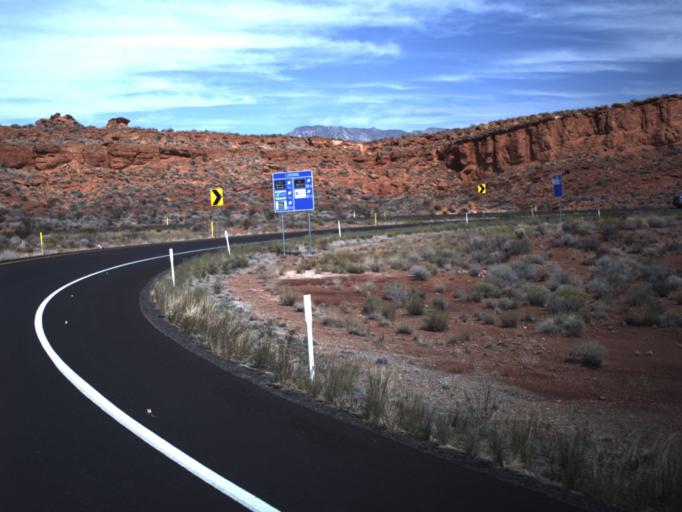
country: US
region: Utah
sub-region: Washington County
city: Washington
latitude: 37.1665
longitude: -113.4540
